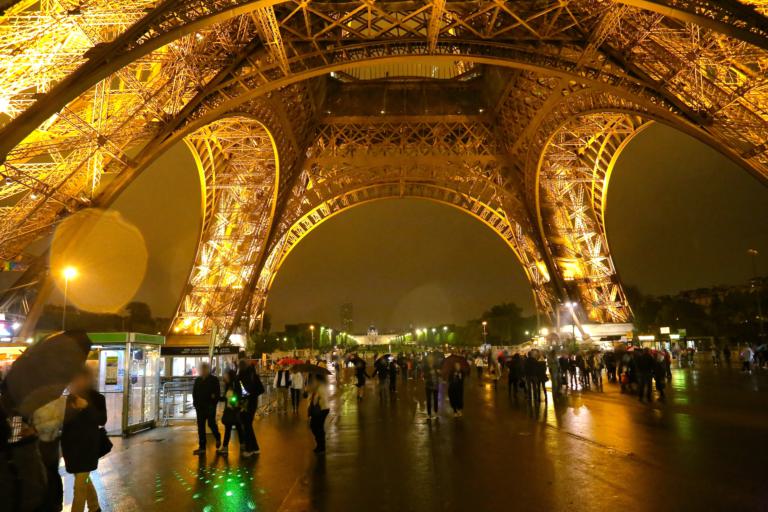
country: FR
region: Ile-de-France
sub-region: Departement des Hauts-de-Seine
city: Neuilly-sur-Seine
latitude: 48.8589
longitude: 2.2938
